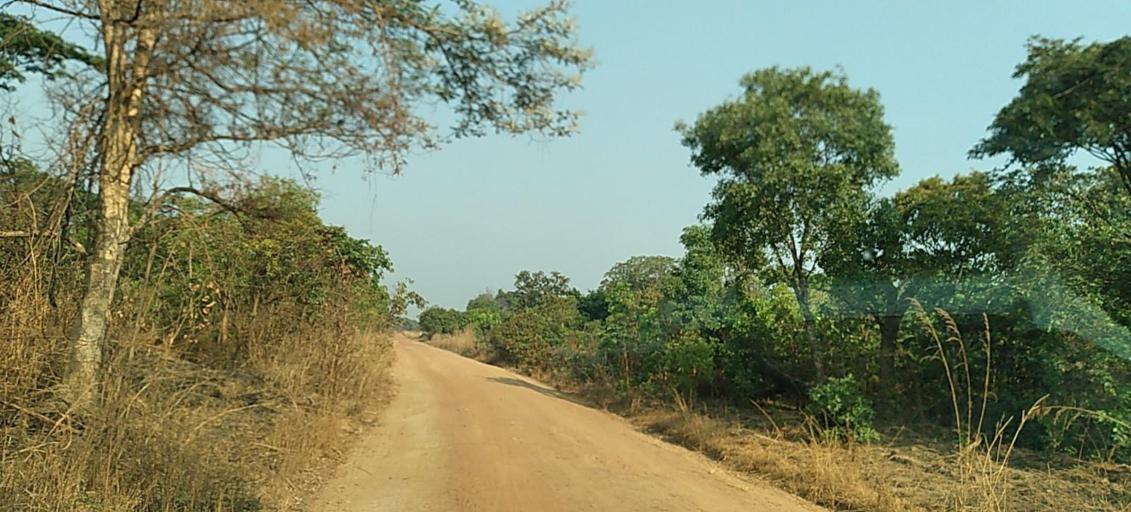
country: ZM
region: Copperbelt
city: Chingola
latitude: -12.8578
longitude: 27.5655
